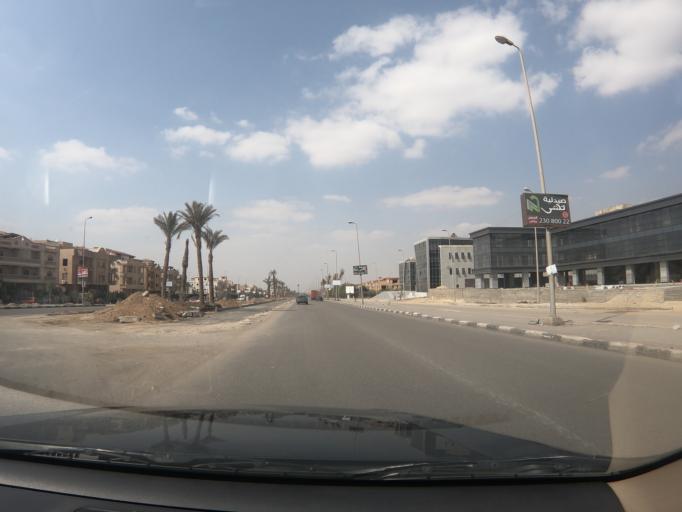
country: EG
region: Muhafazat al Qalyubiyah
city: Al Khankah
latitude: 30.0484
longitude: 31.4750
